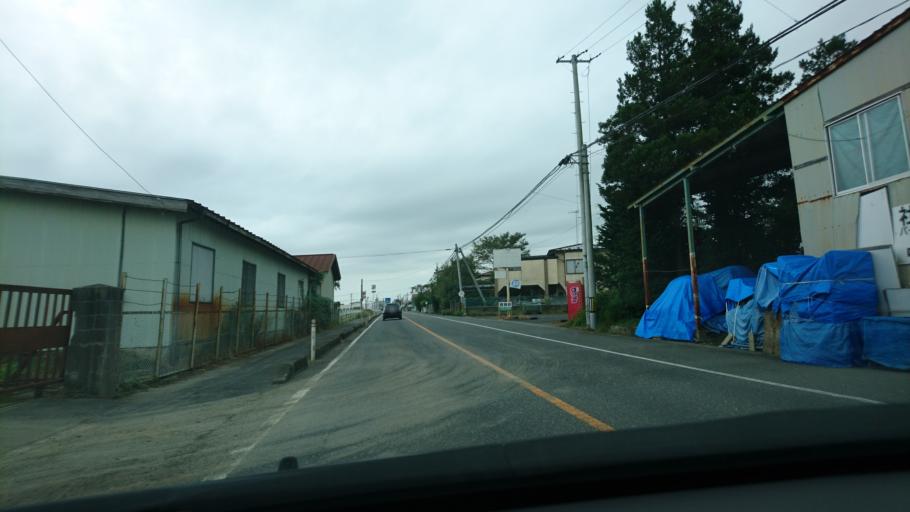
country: JP
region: Iwate
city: Ichinoseki
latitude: 38.7582
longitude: 141.0744
